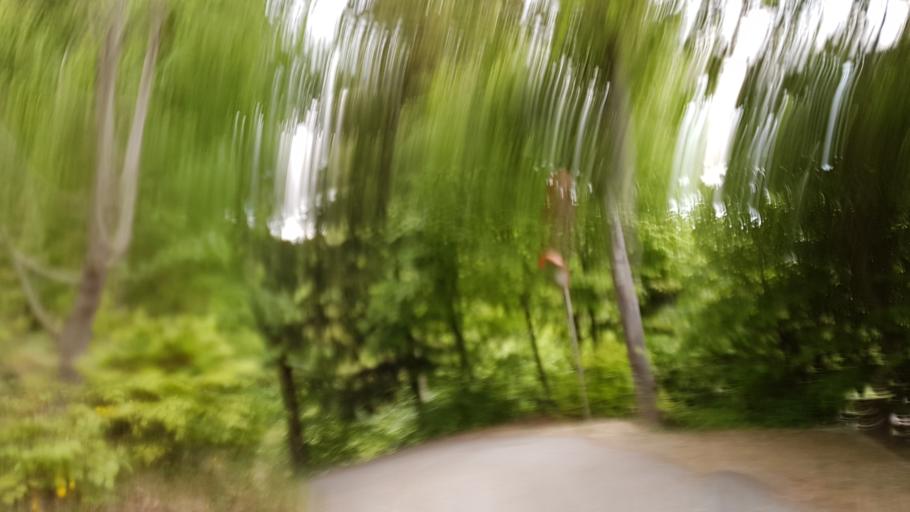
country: CH
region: Bern
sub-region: Bern-Mittelland District
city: Munsingen
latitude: 46.8615
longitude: 7.5487
